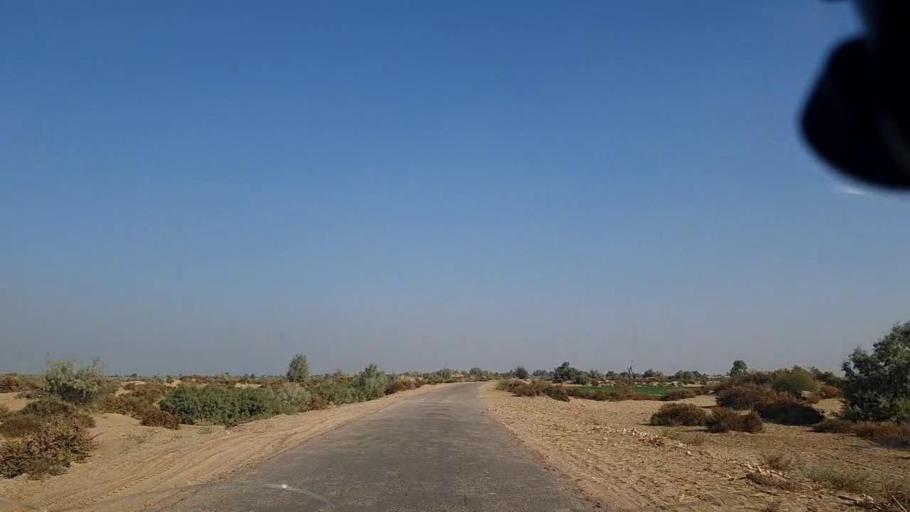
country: PK
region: Sindh
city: Khanpur
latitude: 27.6866
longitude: 69.4722
